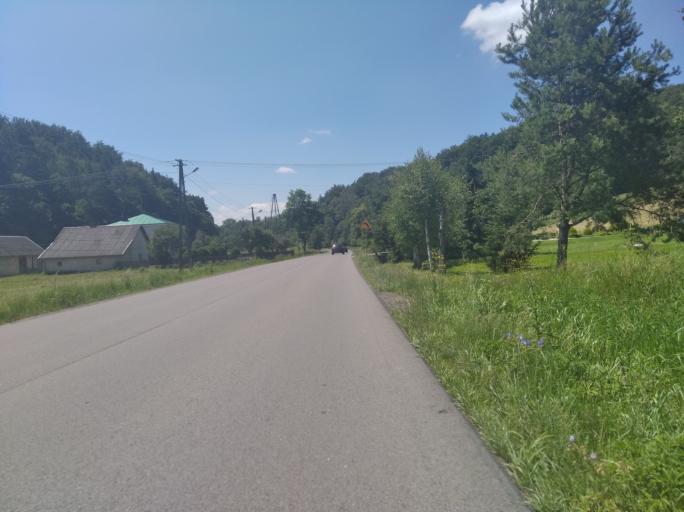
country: PL
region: Subcarpathian Voivodeship
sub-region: Powiat brzozowski
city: Grabownica Starzenska
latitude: 49.6715
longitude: 22.0875
